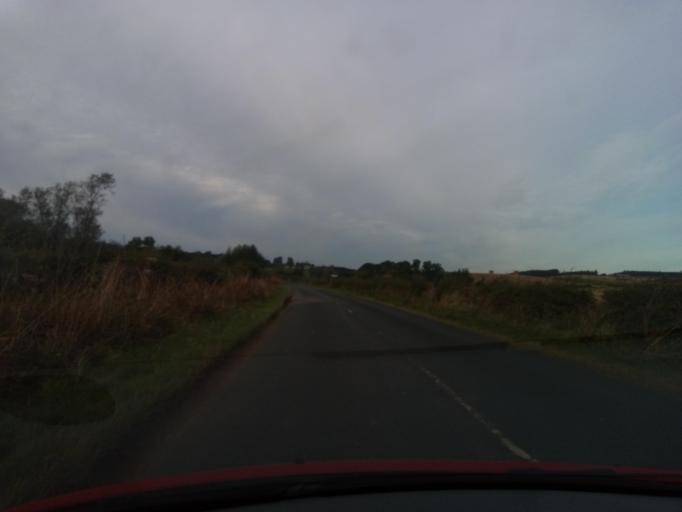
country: GB
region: Scotland
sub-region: The Scottish Borders
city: Kelso
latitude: 55.5221
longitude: -2.3997
